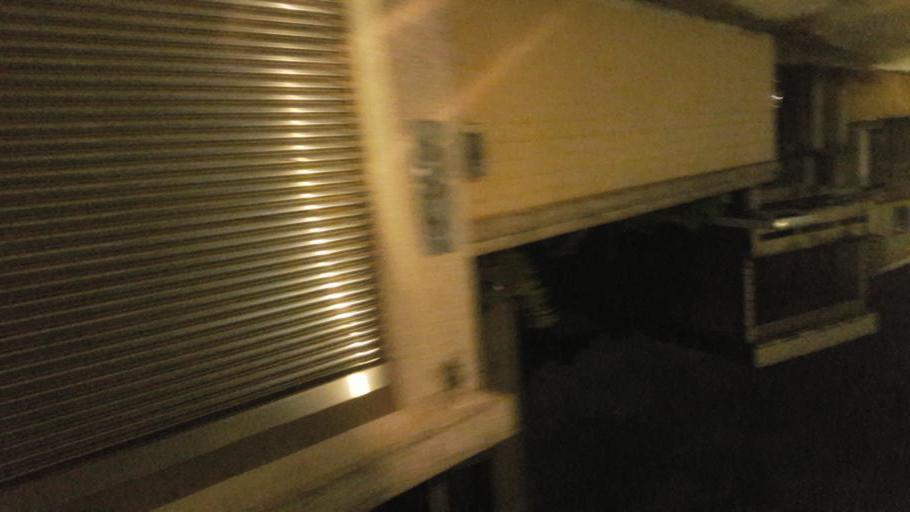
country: TW
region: Taiwan
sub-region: Hsinchu
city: Hsinchu
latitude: 24.7550
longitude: 120.9730
